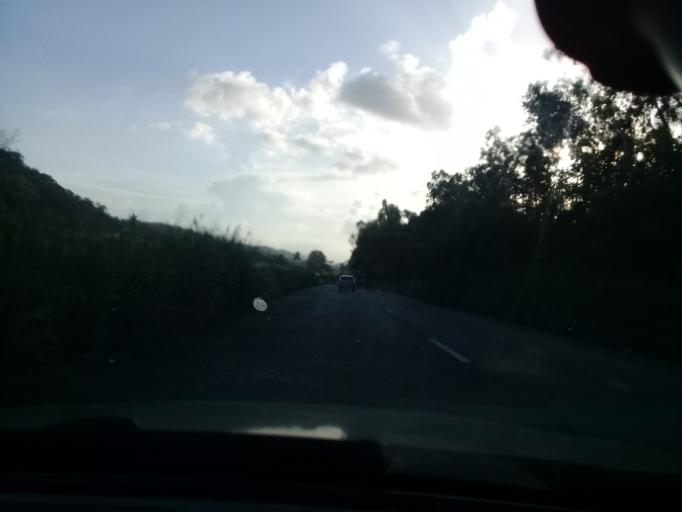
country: BR
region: Pernambuco
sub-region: Moreno
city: Moreno
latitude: -8.1053
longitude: -35.1746
